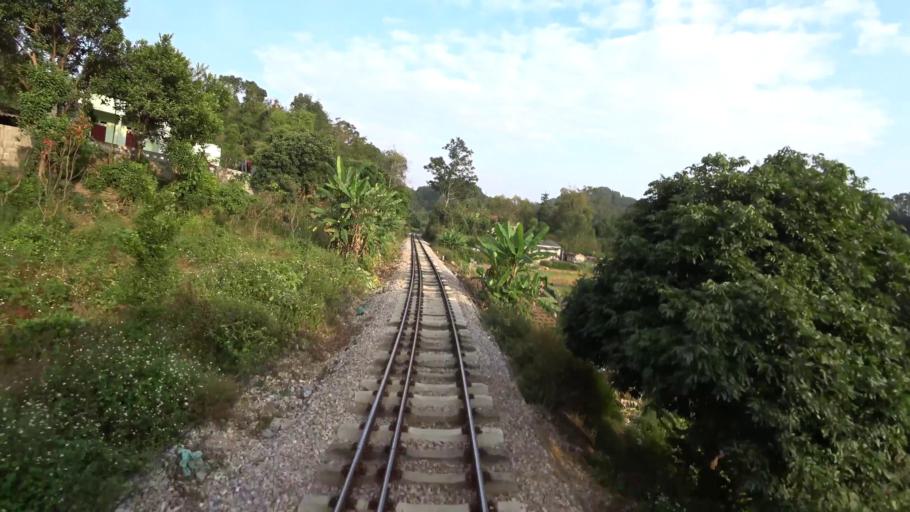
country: VN
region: Lang Son
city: Thi Tran Cao Loc
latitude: 21.9269
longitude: 106.7058
